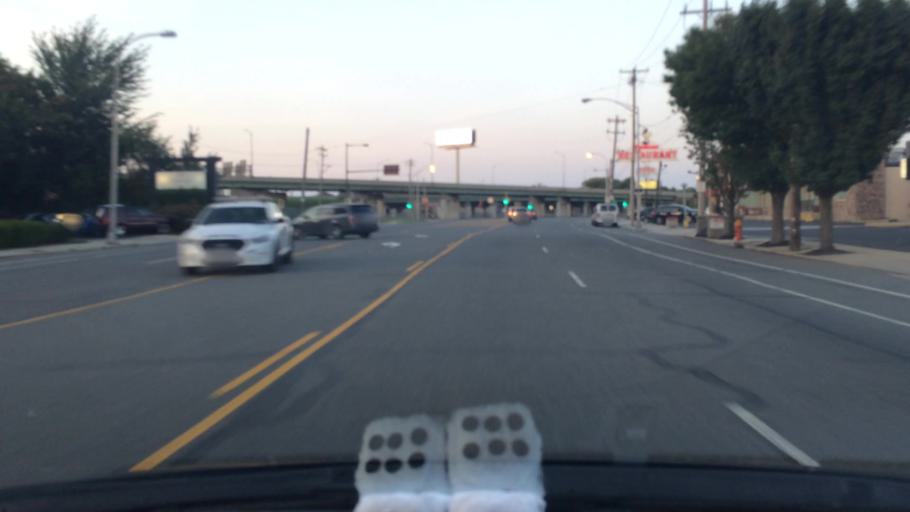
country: US
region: Pennsylvania
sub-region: Philadelphia County
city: Philadelphia
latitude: 39.9120
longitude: -75.1838
